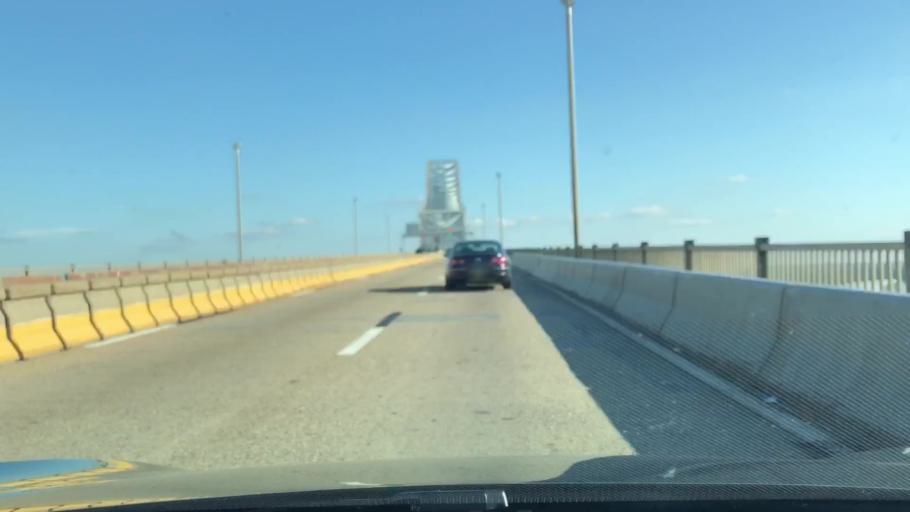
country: US
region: Pennsylvania
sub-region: Delaware County
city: Upland
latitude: 39.8349
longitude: -75.3785
